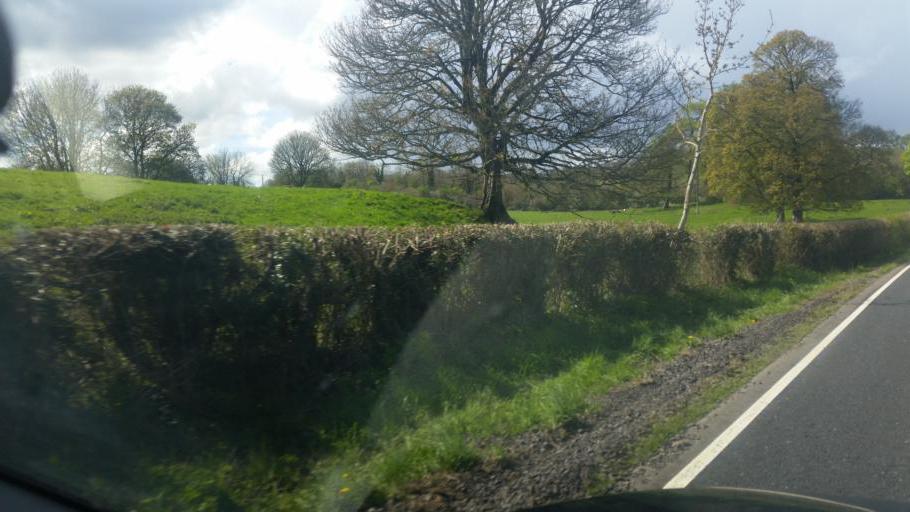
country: GB
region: Northern Ireland
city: Irvinestown
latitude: 54.4380
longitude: -7.7923
